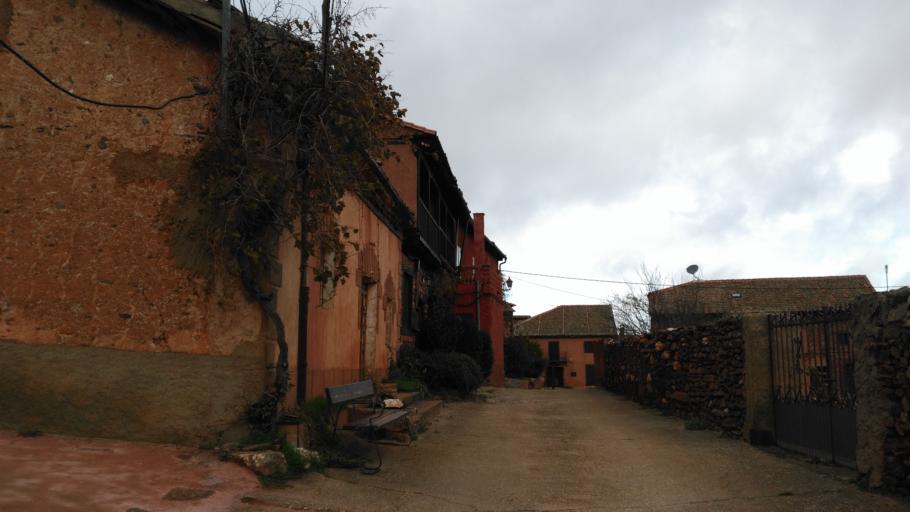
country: ES
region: Castille and Leon
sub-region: Provincia de Soria
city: Liceras
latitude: 41.3142
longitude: -3.3313
